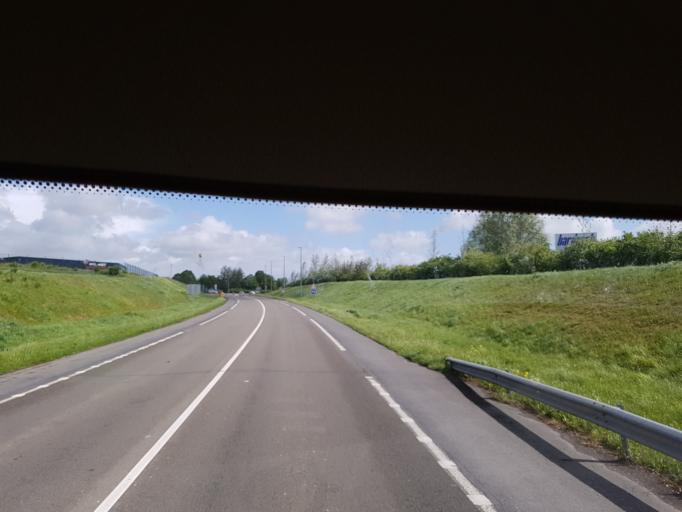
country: FR
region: Nord-Pas-de-Calais
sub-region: Departement du Nord
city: Proville
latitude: 50.1725
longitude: 3.1958
